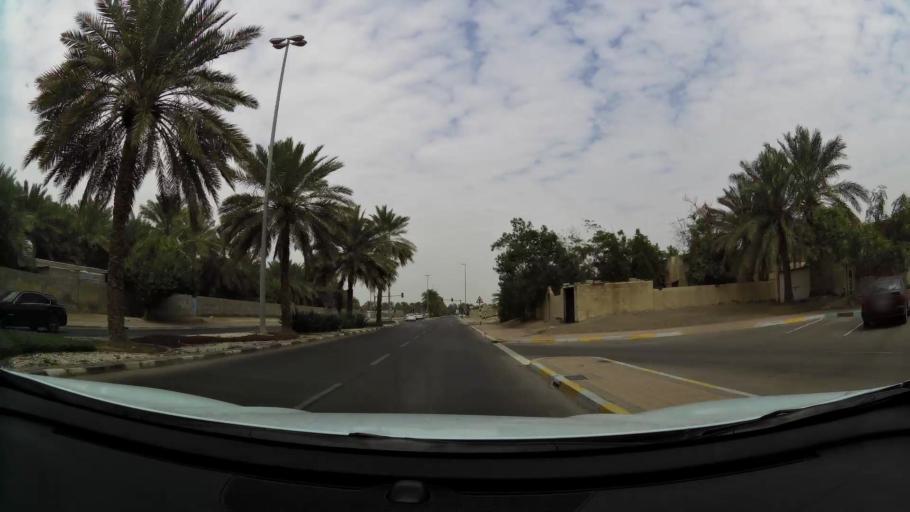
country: OM
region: Al Buraimi
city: Al Buraymi
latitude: 24.2247
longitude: 55.7798
